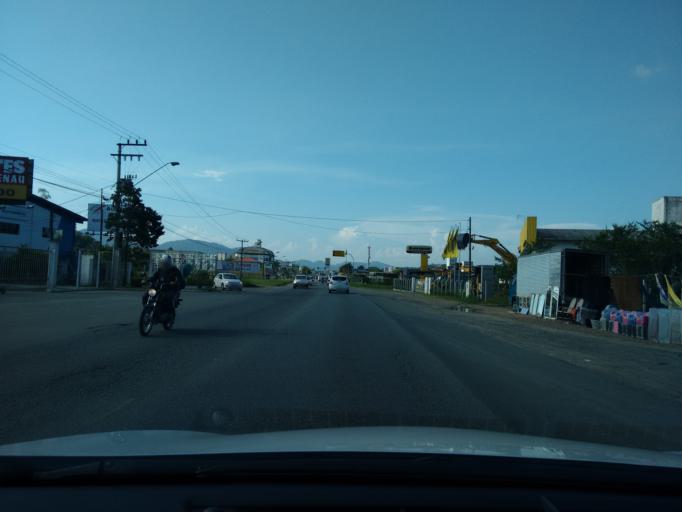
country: BR
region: Santa Catarina
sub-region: Blumenau
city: Blumenau
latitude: -26.8562
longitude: -49.0861
